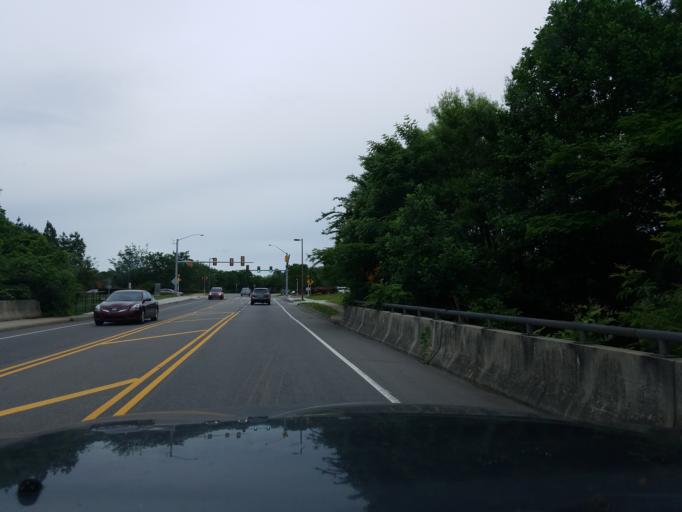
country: US
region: North Carolina
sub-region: Durham County
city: Durham
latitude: 36.0283
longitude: -78.9172
